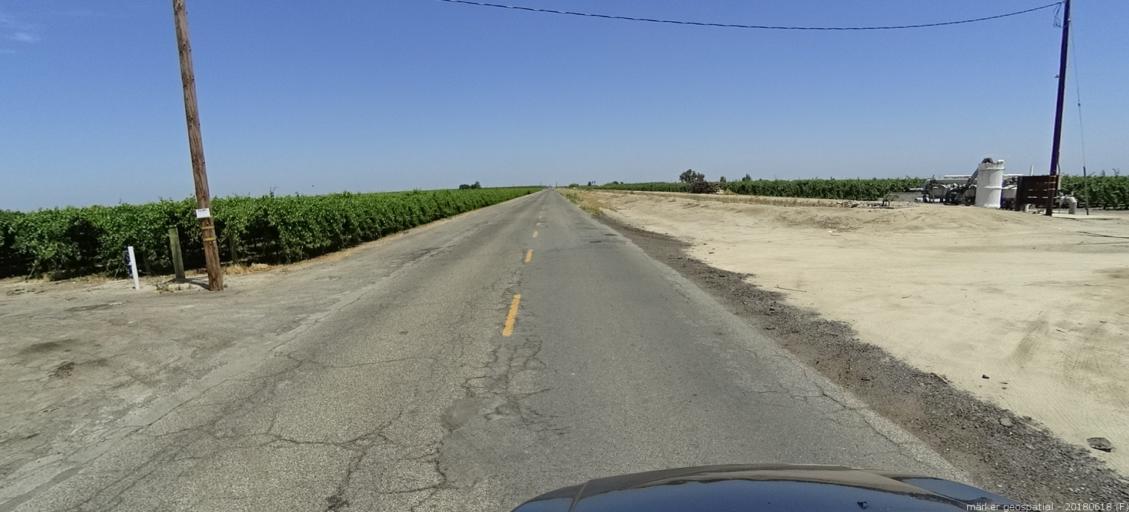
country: US
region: California
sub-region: Madera County
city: Parkwood
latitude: 36.8874
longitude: -120.1286
